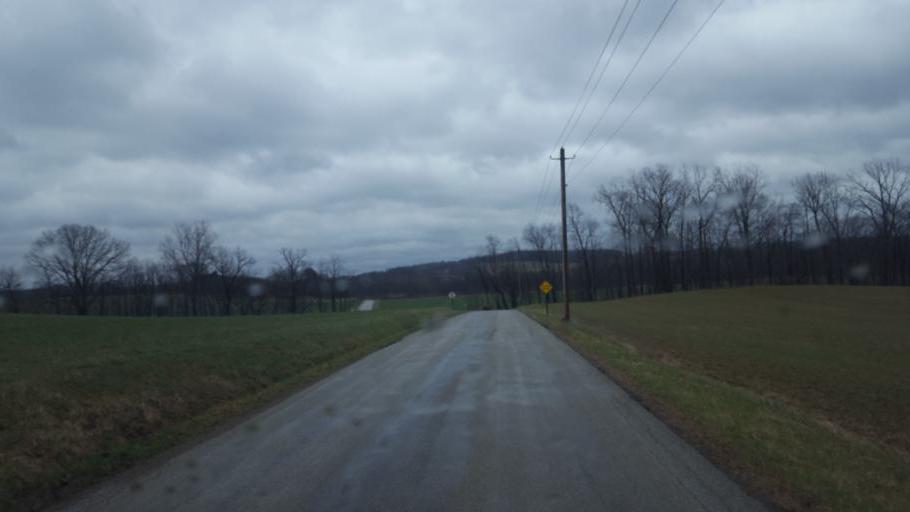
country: US
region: Ohio
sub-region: Sandusky County
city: Bellville
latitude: 40.5563
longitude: -82.4872
